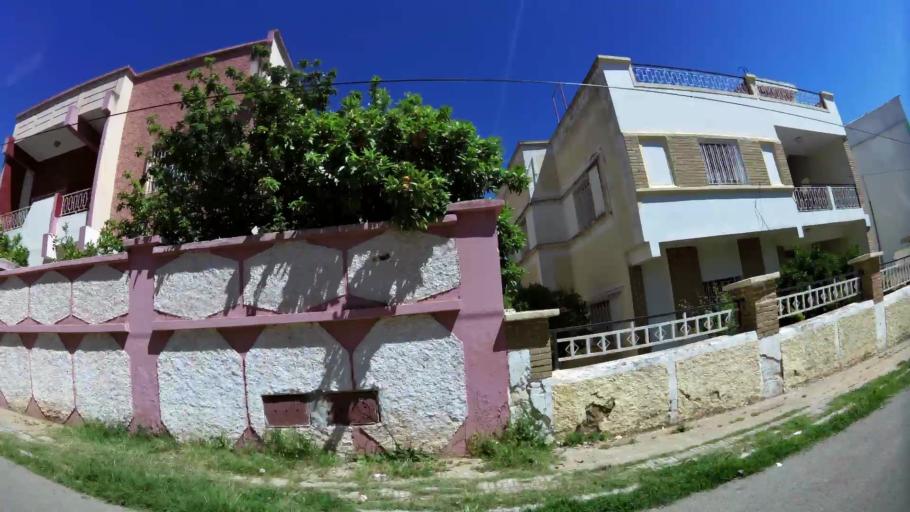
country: MA
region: Meknes-Tafilalet
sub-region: Meknes
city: Meknes
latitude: 33.9025
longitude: -5.5274
